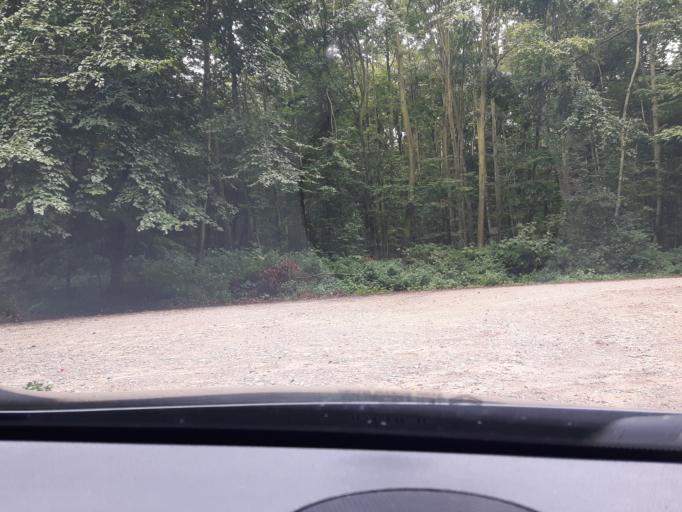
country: DK
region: Central Jutland
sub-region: Hedensted Kommune
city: Hornsyld
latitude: 55.6808
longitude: 9.8584
